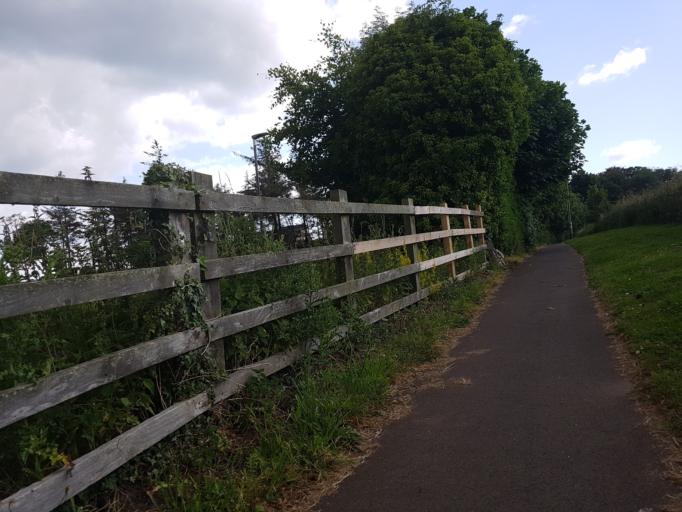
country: GB
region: England
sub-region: Northumberland
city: Alnmouth
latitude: 55.3960
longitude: -1.6339
